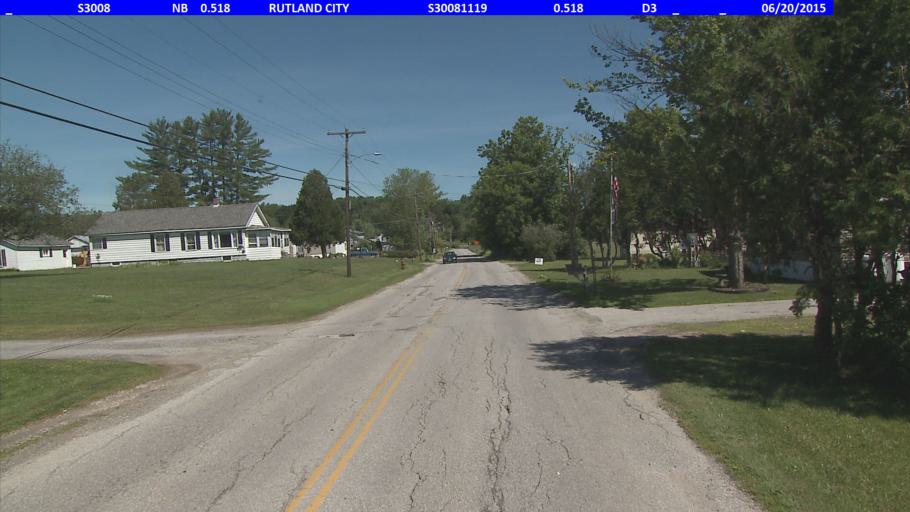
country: US
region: Vermont
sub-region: Rutland County
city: Rutland
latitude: 43.5940
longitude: -72.9928
